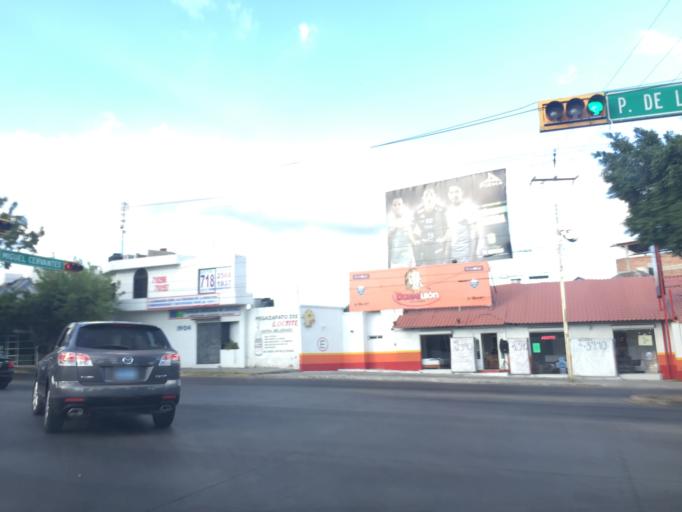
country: MX
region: Guanajuato
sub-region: Leon
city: La Ermita
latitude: 21.1464
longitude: -101.7014
